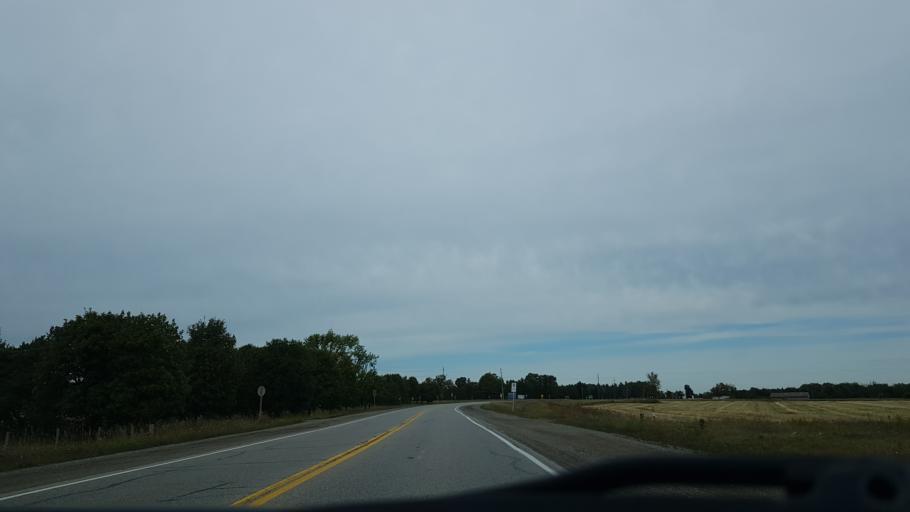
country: CA
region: Ontario
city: Orangeville
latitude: 43.8258
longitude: -80.0347
